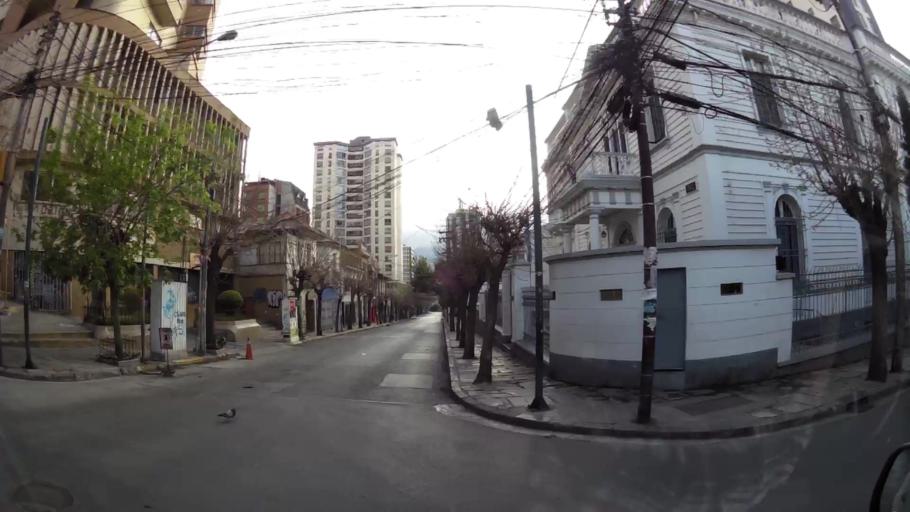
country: BO
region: La Paz
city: La Paz
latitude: -16.5082
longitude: -68.1302
